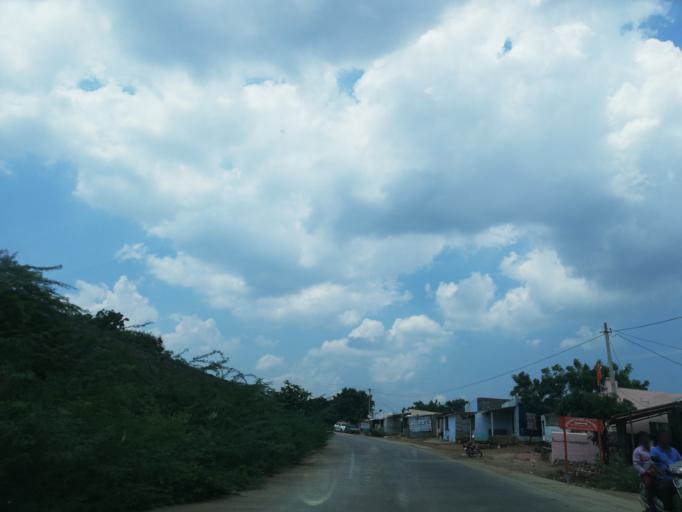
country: IN
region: Andhra Pradesh
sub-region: Guntur
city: Macherla
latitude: 16.5819
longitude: 79.3285
